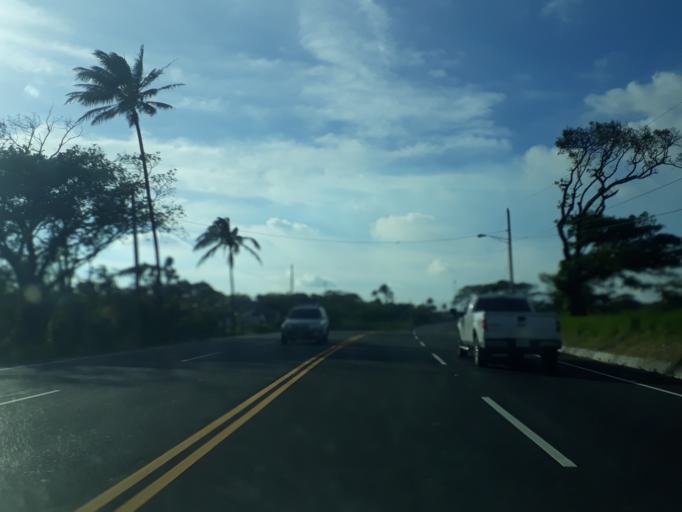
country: NI
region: Carazo
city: Diriamba
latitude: 11.9190
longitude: -86.2773
